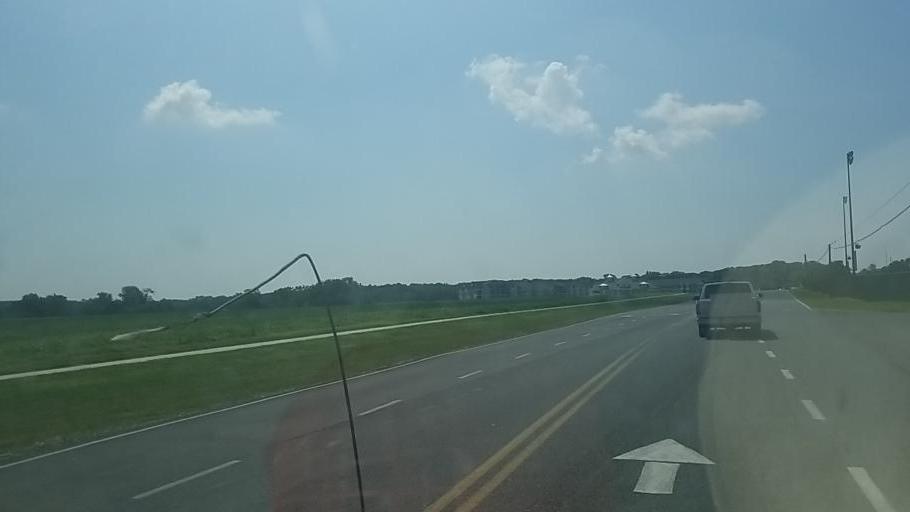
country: US
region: Maryland
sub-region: Worcester County
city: Berlin
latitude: 38.3412
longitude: -75.1889
